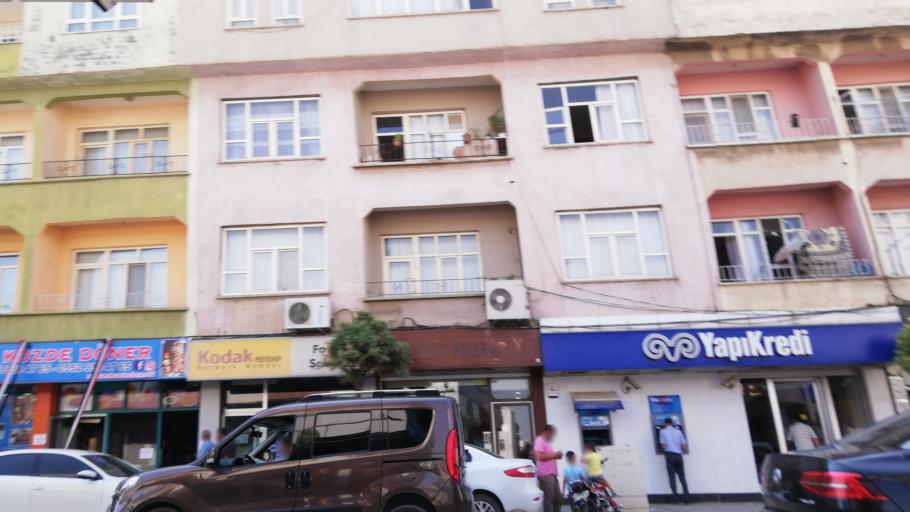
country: TR
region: Mardin
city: Midyat
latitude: 37.4258
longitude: 41.3394
